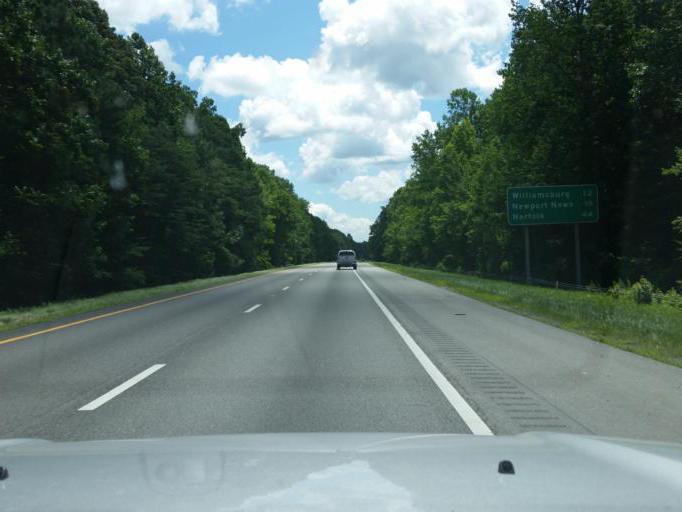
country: US
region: Virginia
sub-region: King William County
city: West Point
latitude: 37.4154
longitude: -76.8062
